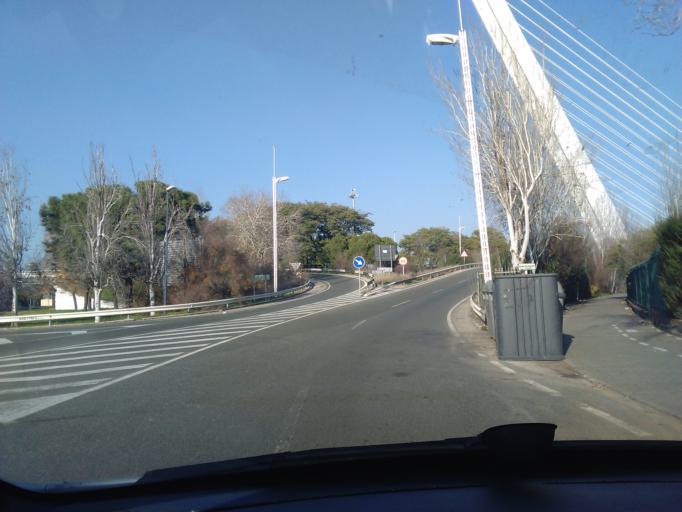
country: ES
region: Andalusia
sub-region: Provincia de Sevilla
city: Sevilla
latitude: 37.4119
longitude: -5.9939
